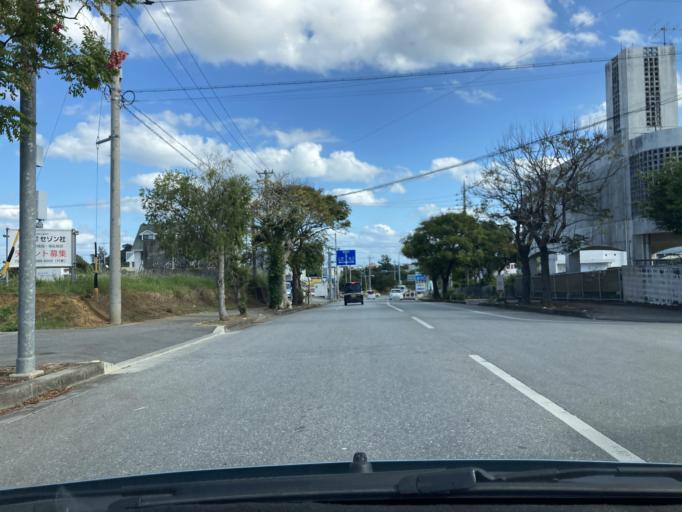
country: JP
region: Okinawa
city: Gushikawa
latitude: 26.3736
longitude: 127.8257
